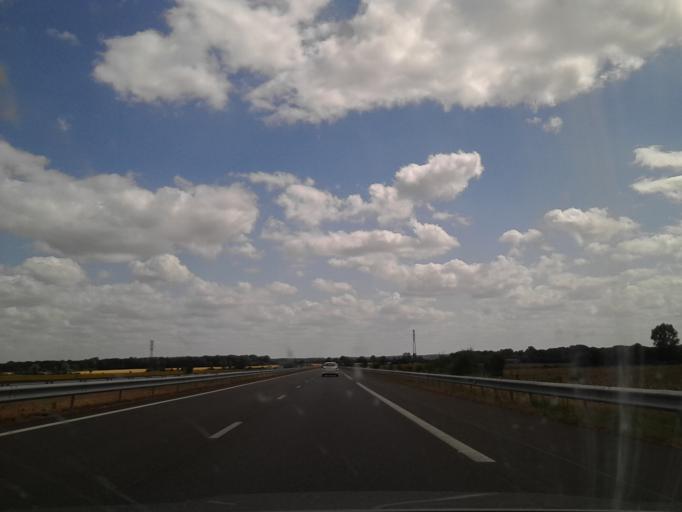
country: FR
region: Centre
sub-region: Departement du Cher
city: Chateauneuf-sur-Cher
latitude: 46.8166
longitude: 2.4127
